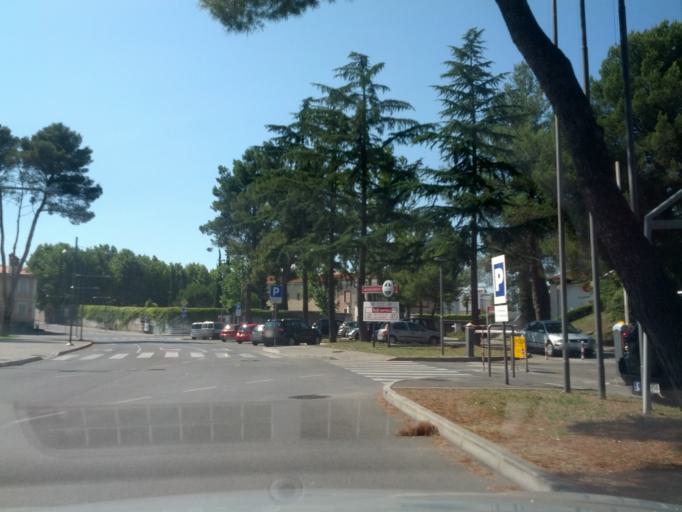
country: SI
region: Koper-Capodistria
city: Koper
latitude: 45.5477
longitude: 13.7374
